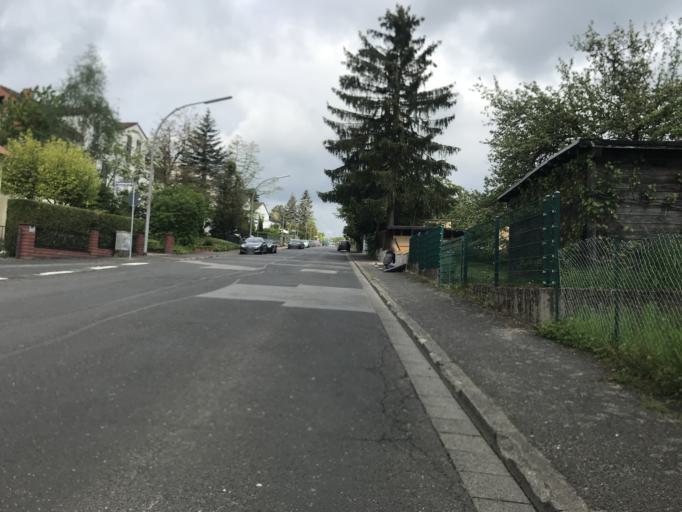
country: DE
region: Hesse
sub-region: Regierungsbezirk Darmstadt
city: Walluf
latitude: 50.0598
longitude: 8.1901
